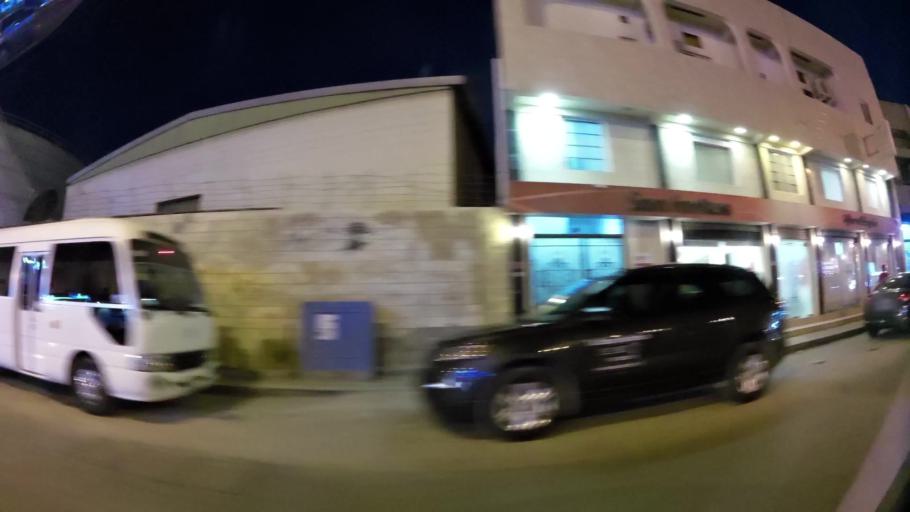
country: BH
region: Manama
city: Jidd Hafs
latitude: 26.2114
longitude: 50.5434
